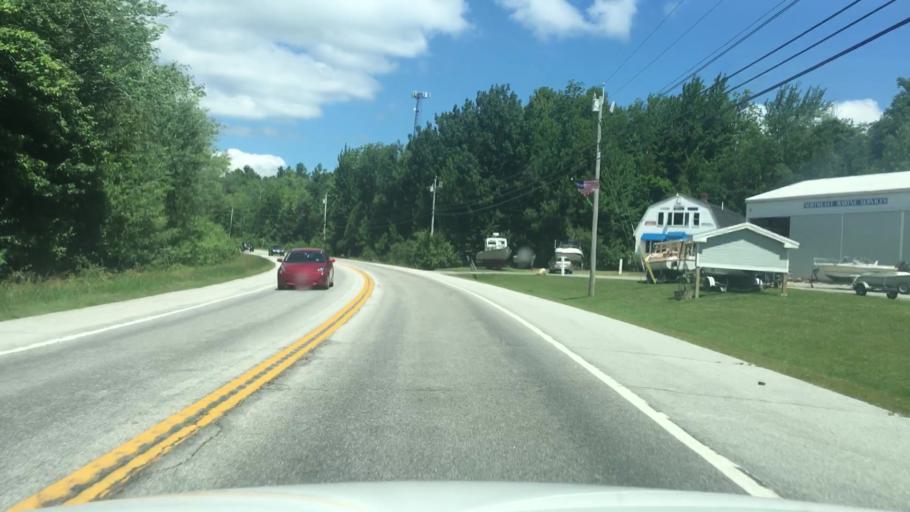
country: US
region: Maine
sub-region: Waldo County
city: Northport
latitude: 44.3540
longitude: -68.9675
